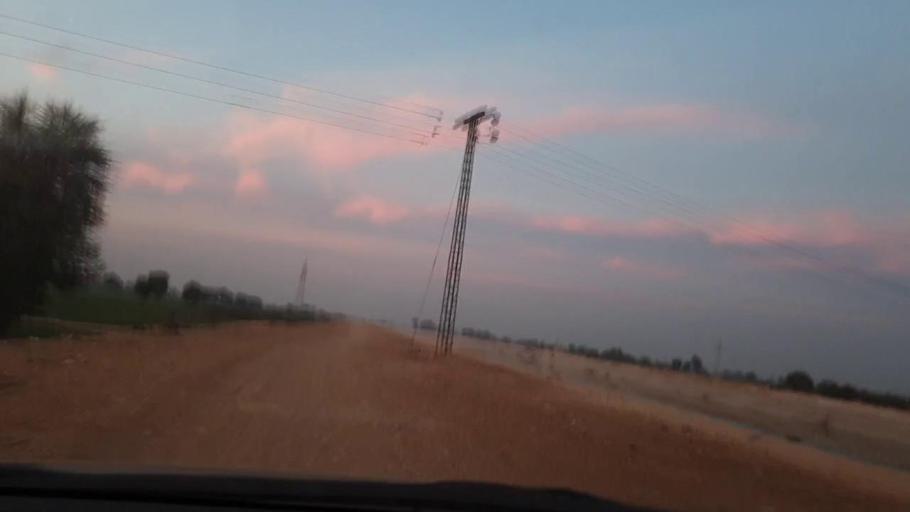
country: PK
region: Sindh
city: Sakrand
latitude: 26.1991
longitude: 68.3050
